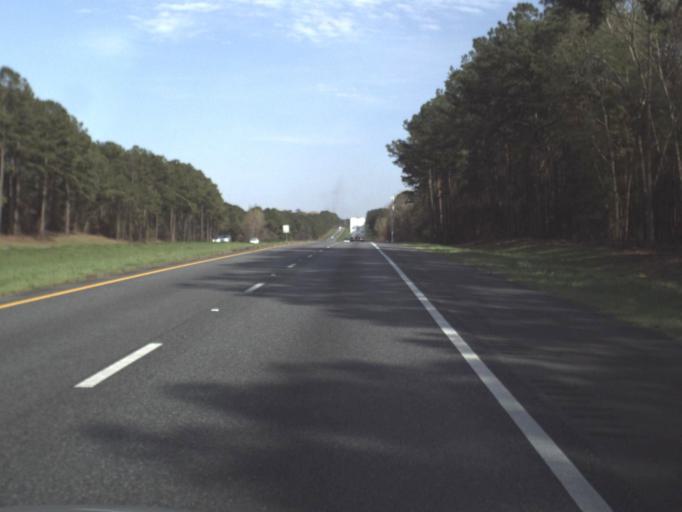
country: US
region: Florida
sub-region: Leon County
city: Tallahassee
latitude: 30.4981
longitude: -84.2028
